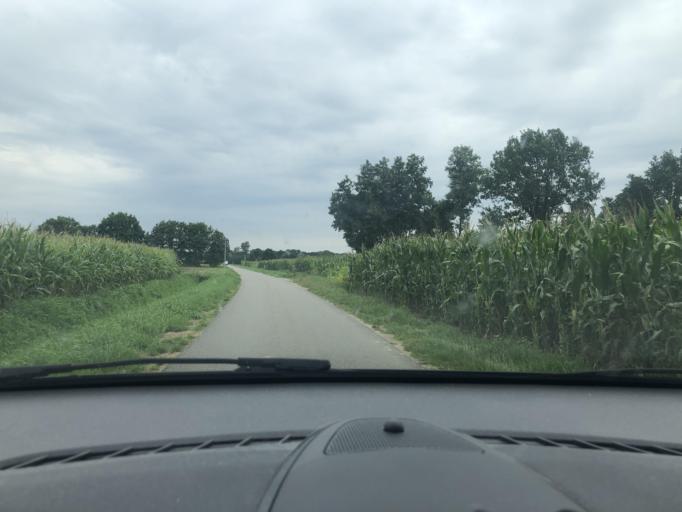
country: DE
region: Mecklenburg-Vorpommern
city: Nostorf
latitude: 53.3566
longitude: 10.6551
